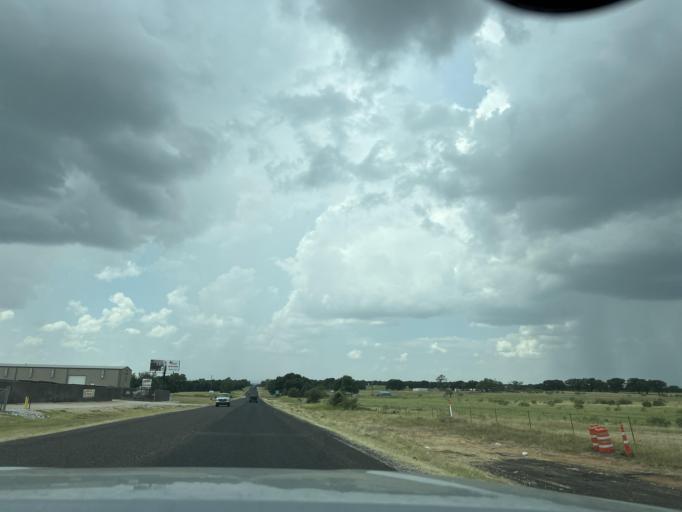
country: US
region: Texas
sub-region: Wise County
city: Decatur
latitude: 33.1739
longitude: -97.6223
